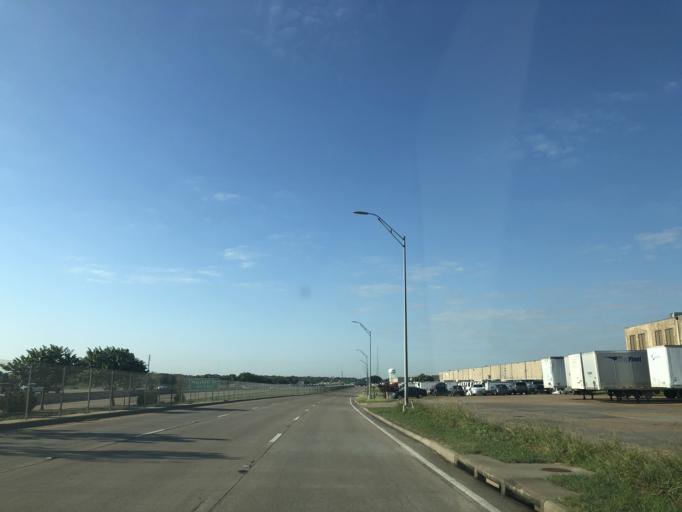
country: US
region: Texas
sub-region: Dallas County
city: Grand Prairie
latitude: 32.7393
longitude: -97.0204
